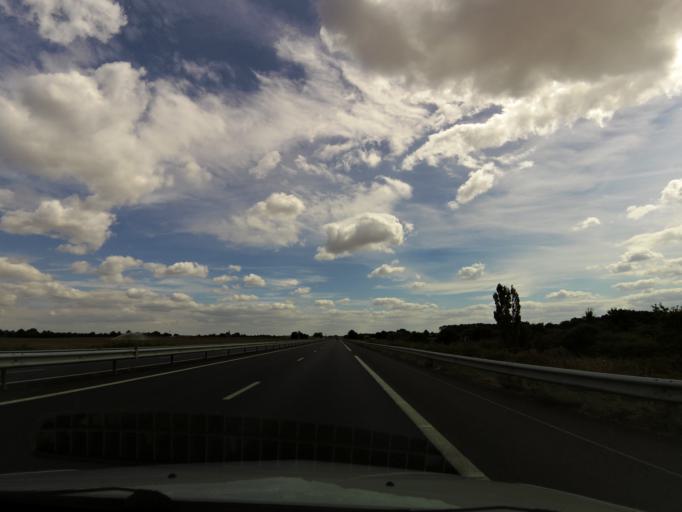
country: FR
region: Pays de la Loire
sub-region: Departement de la Vendee
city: Bouffere
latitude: 46.9306
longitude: -1.3387
